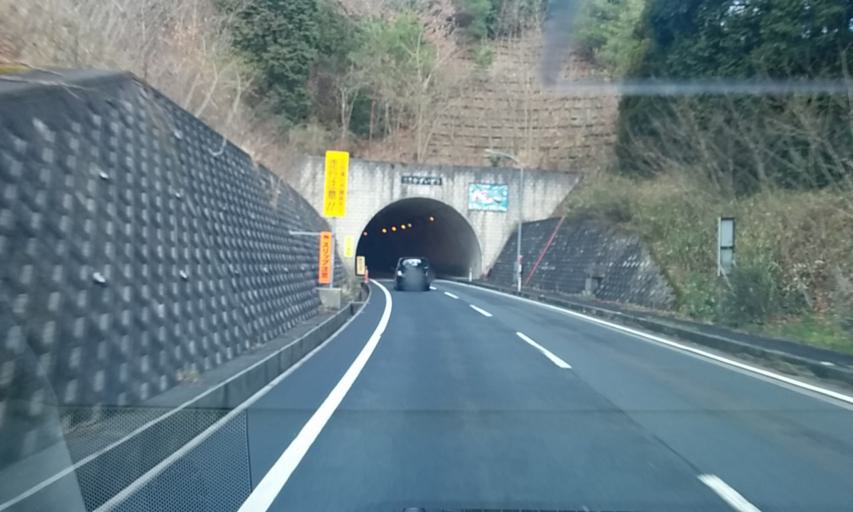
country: JP
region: Kyoto
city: Miyazu
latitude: 35.5816
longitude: 135.1176
